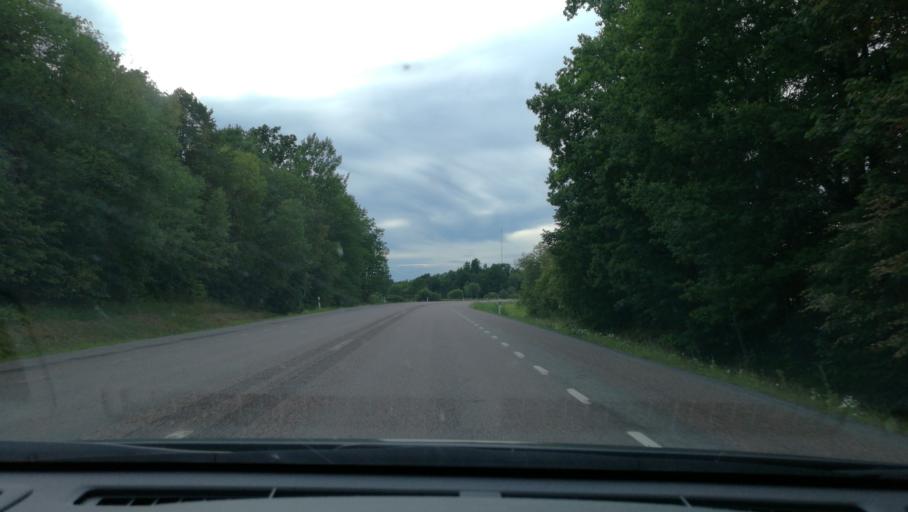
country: SE
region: Vaestmanland
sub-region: Kungsors Kommun
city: Kungsoer
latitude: 59.4370
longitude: 16.0564
